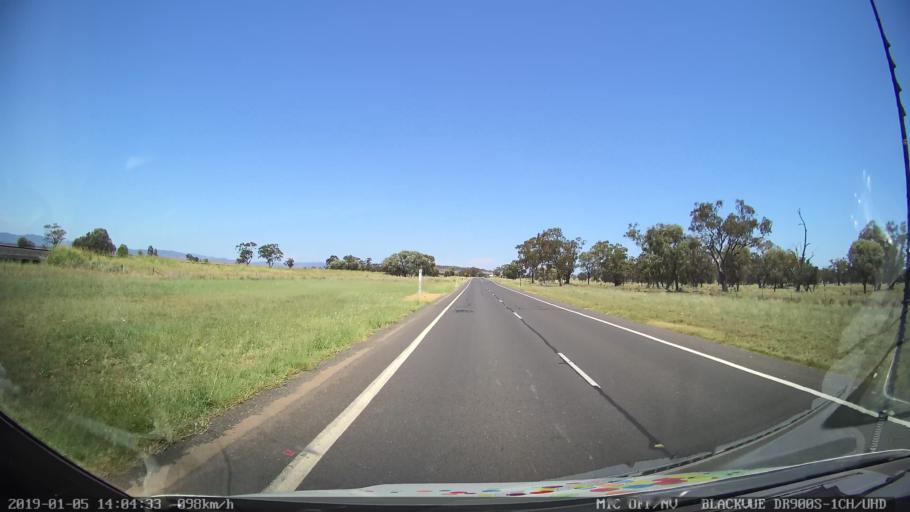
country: AU
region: New South Wales
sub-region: Gunnedah
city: Gunnedah
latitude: -31.2011
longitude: 150.3653
